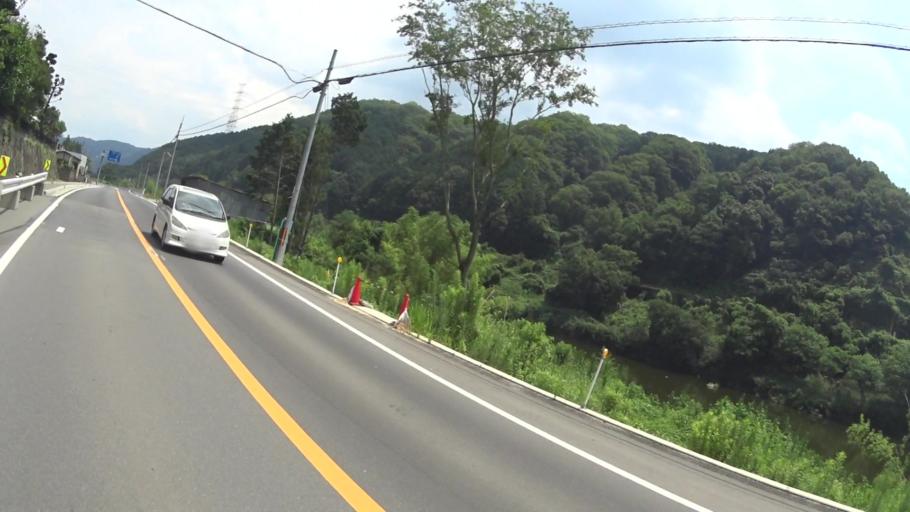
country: JP
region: Nara
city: Nara-shi
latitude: 34.7661
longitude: 135.9109
